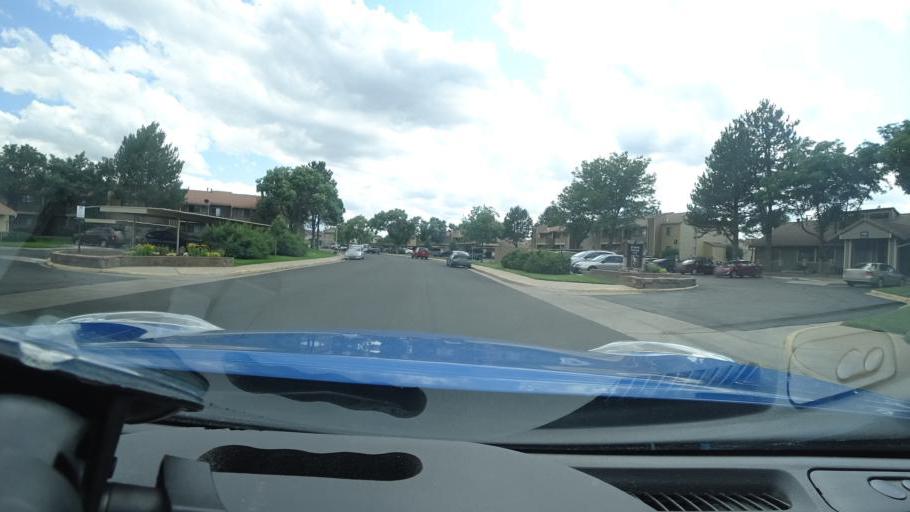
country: US
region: Colorado
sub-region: Adams County
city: Aurora
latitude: 39.6932
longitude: -104.8694
